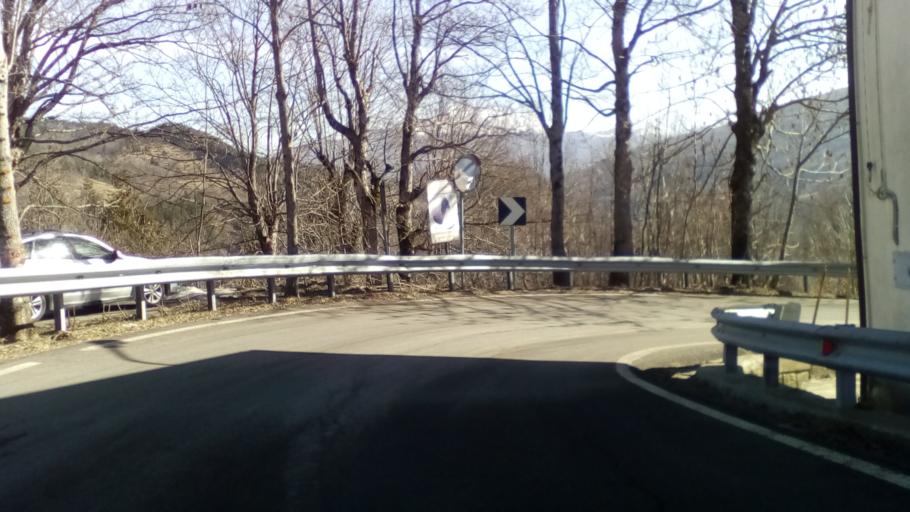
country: IT
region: Emilia-Romagna
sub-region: Provincia di Modena
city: Pievepelago
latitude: 44.1931
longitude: 10.5483
